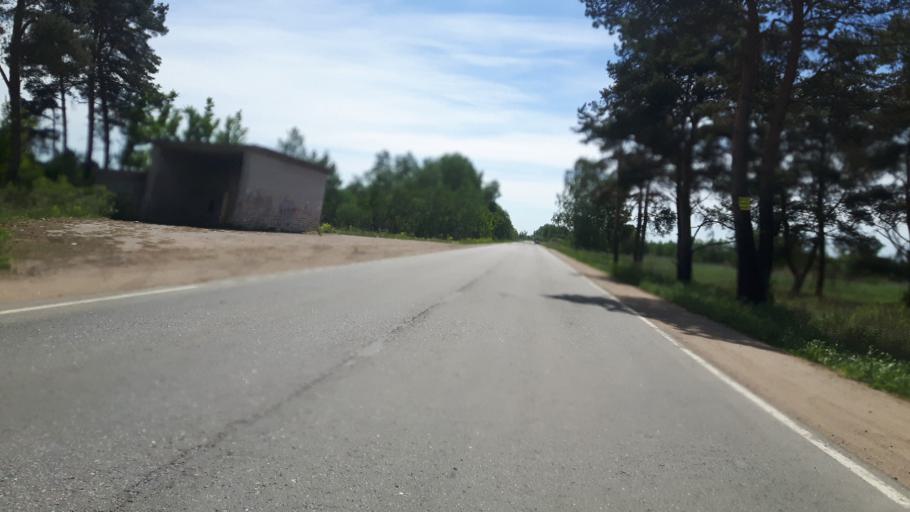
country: RU
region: Leningrad
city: Ust'-Luga
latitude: 59.5773
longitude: 28.1754
